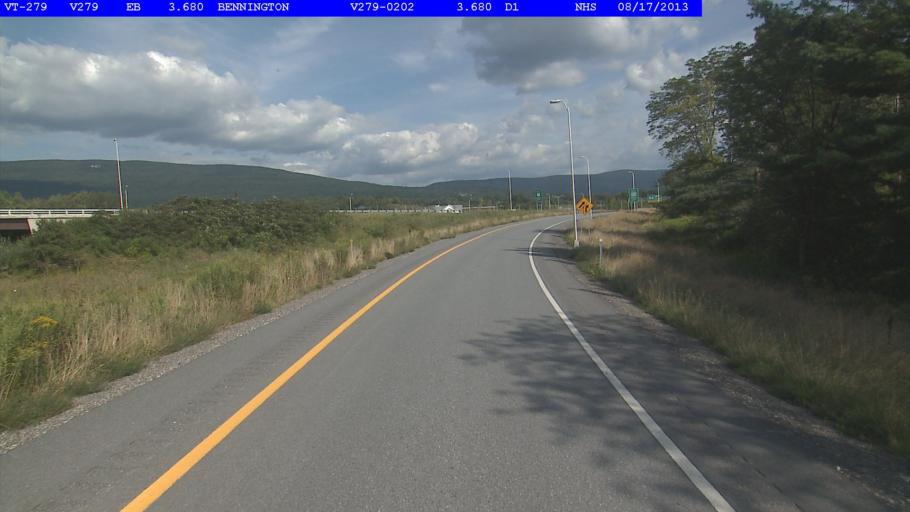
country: US
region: Vermont
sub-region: Bennington County
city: Bennington
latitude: 42.9052
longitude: -73.2094
